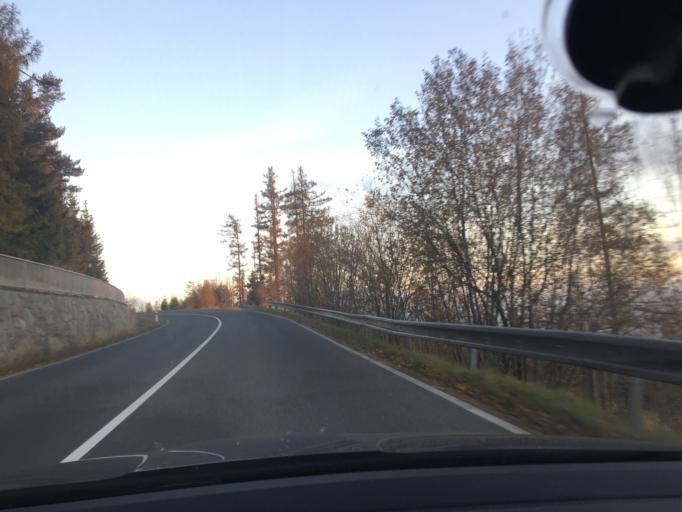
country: SK
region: Presovsky
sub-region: Okres Poprad
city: Svit
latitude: 49.1188
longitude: 20.1451
